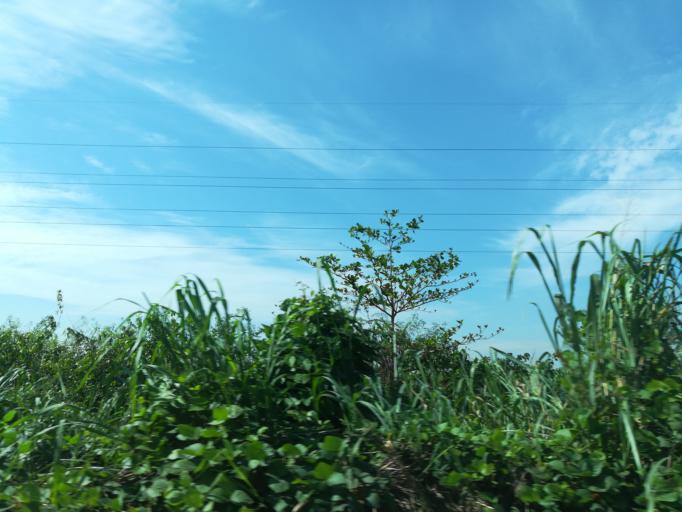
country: NG
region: Lagos
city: Ebute Ikorodu
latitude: 6.6213
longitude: 3.4531
